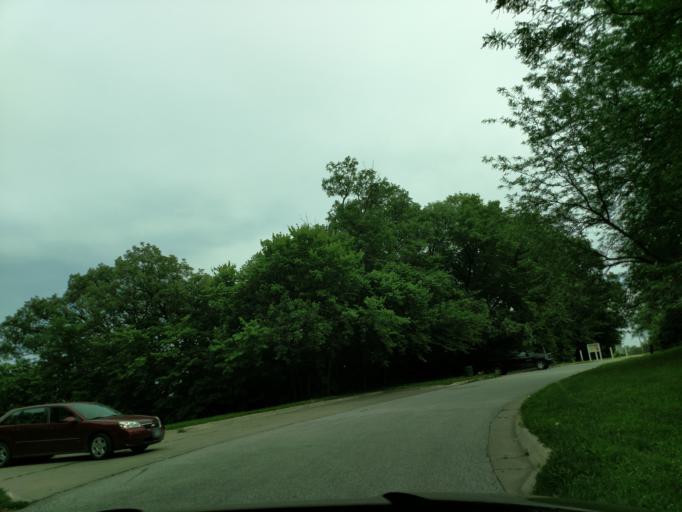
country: US
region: Nebraska
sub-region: Douglas County
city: Omaha
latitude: 41.2007
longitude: -95.9326
